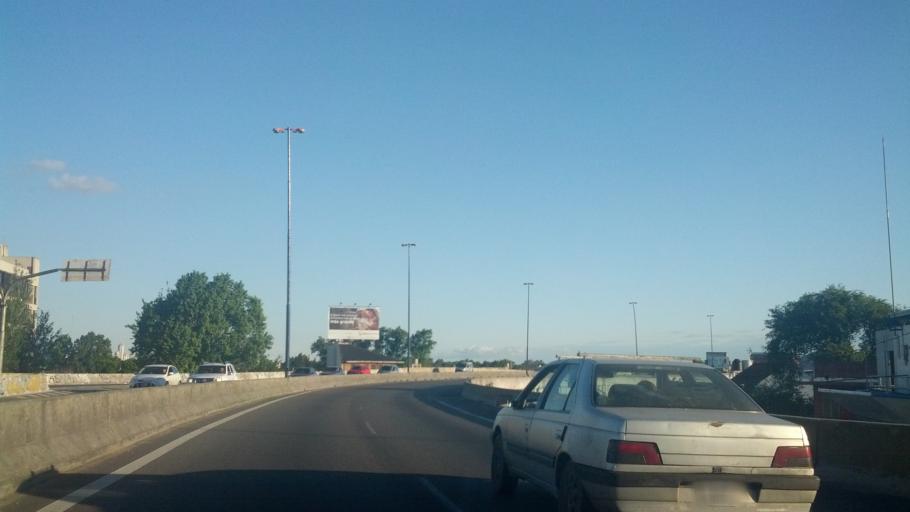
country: AR
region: Buenos Aires
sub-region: Partido de Lomas de Zamora
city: Lomas de Zamora
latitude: -34.7430
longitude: -58.4301
